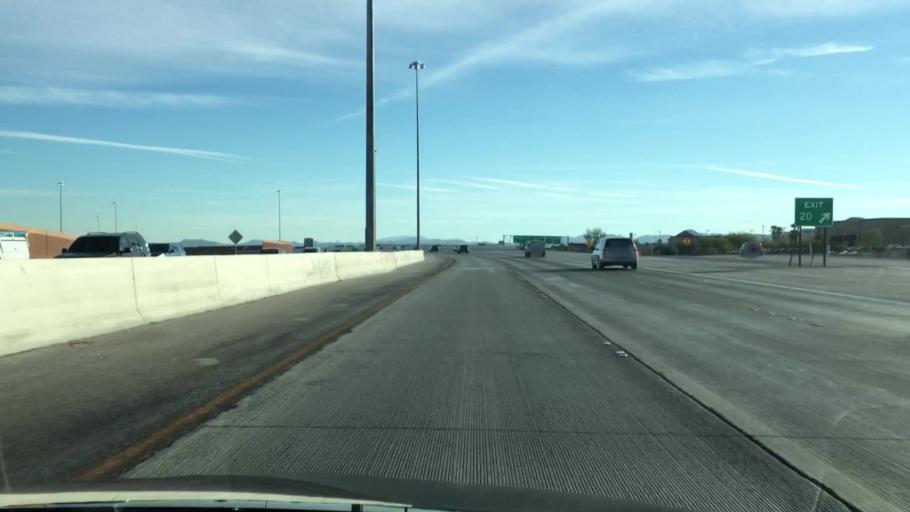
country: US
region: Nevada
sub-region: Clark County
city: Summerlin South
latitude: 36.1036
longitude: -115.2953
